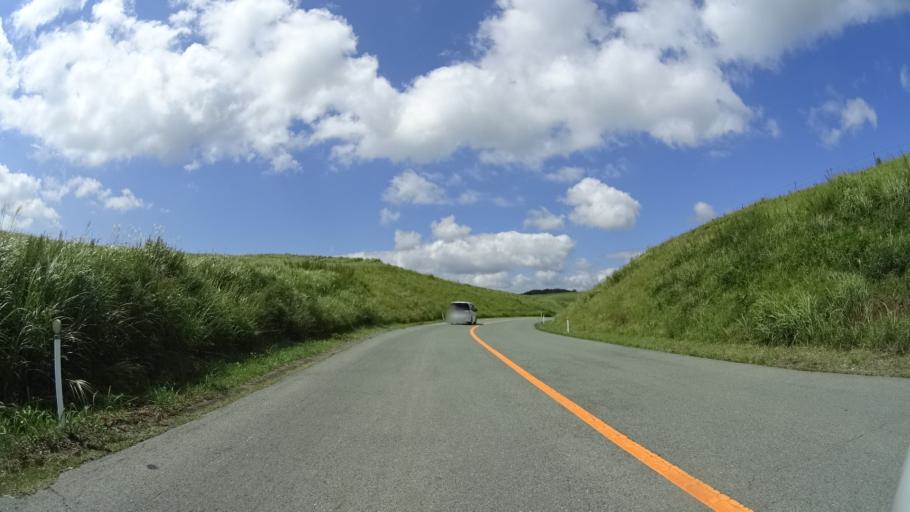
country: JP
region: Kumamoto
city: Aso
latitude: 33.0026
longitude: 131.1327
